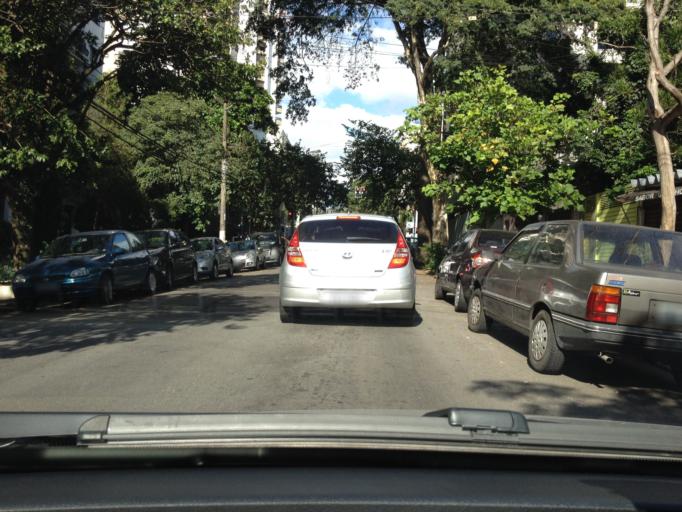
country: BR
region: Sao Paulo
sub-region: Sao Paulo
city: Sao Paulo
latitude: -23.5511
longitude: -46.6903
